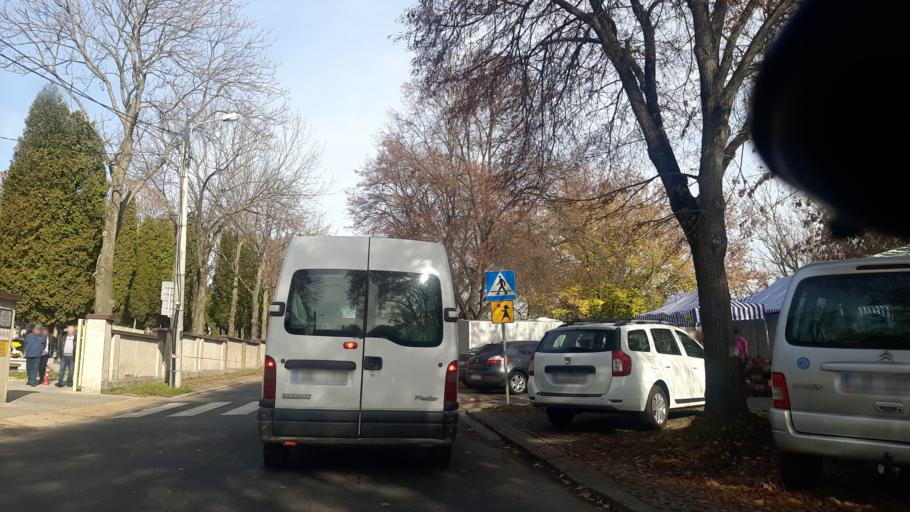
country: PL
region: Lublin Voivodeship
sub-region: Powiat lubelski
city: Lublin
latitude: 51.2605
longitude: 22.5799
